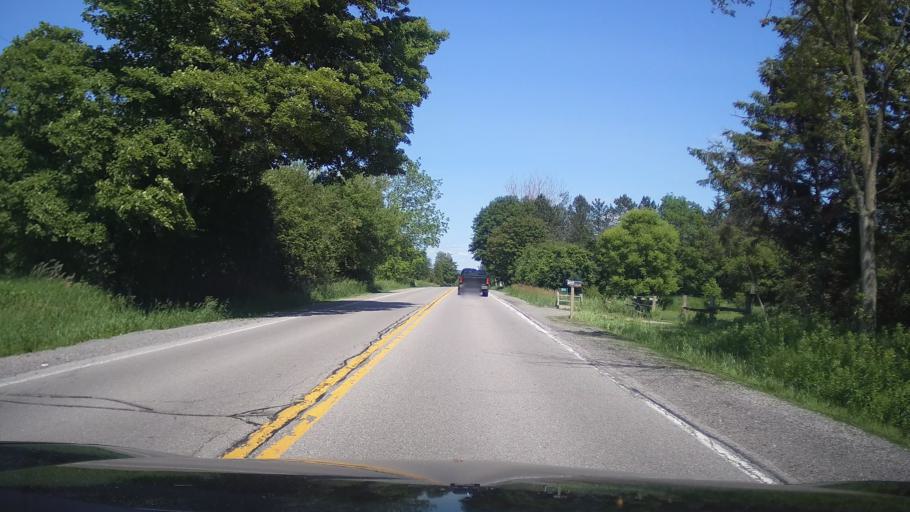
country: CA
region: Ontario
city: Oshawa
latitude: 44.0074
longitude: -78.8038
